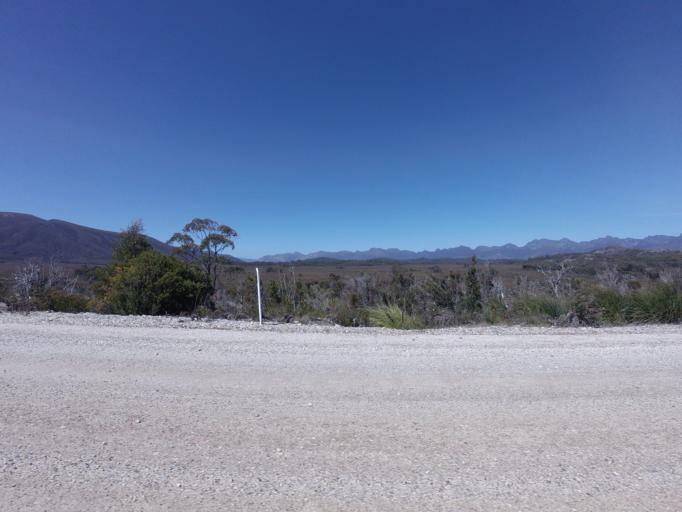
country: AU
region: Tasmania
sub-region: Huon Valley
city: Geeveston
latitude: -43.0373
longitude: 146.3312
